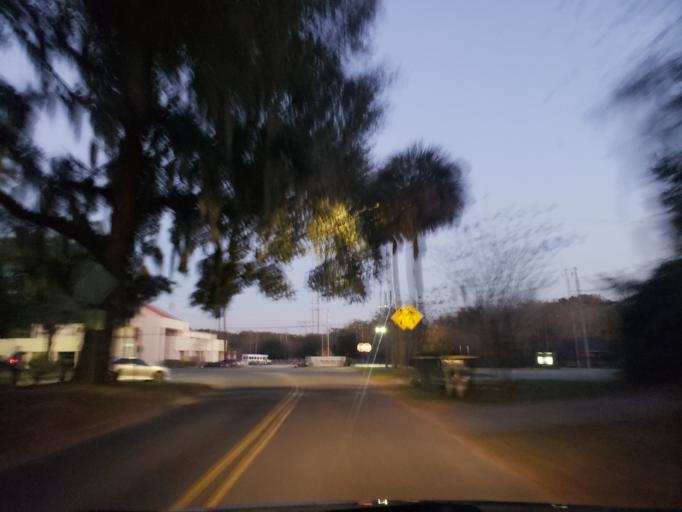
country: US
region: Georgia
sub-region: Chatham County
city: Thunderbolt
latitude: 32.0427
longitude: -81.0786
